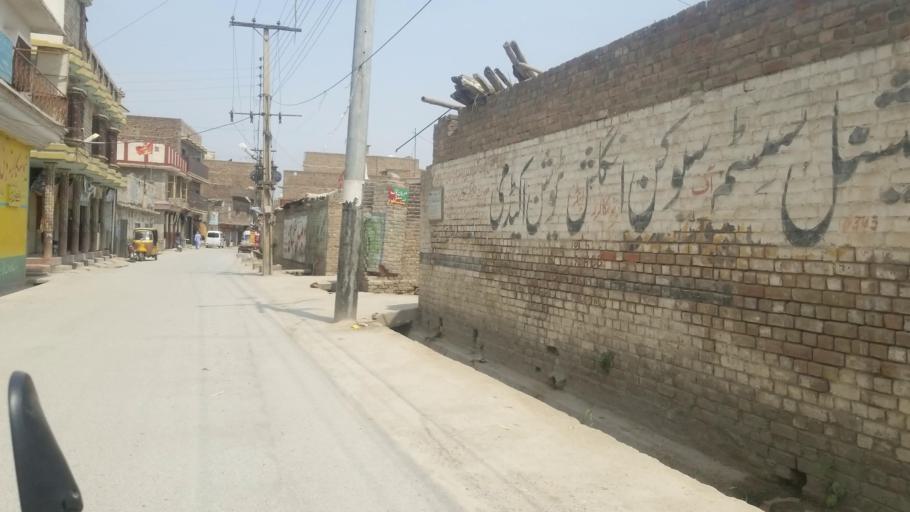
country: PK
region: Khyber Pakhtunkhwa
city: Peshawar
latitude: 34.0274
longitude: 71.5884
